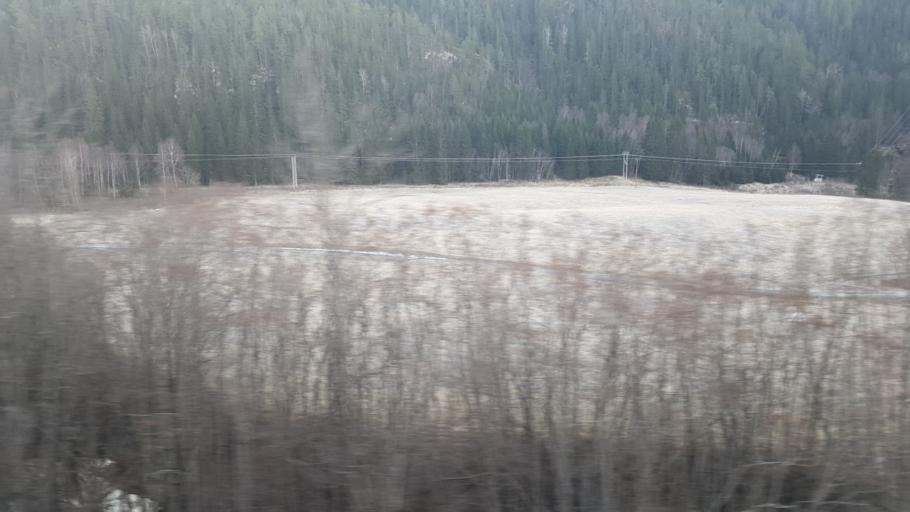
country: NO
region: Nord-Trondelag
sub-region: Stjordal
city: Stjordalshalsen
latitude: 63.5966
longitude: 11.0198
